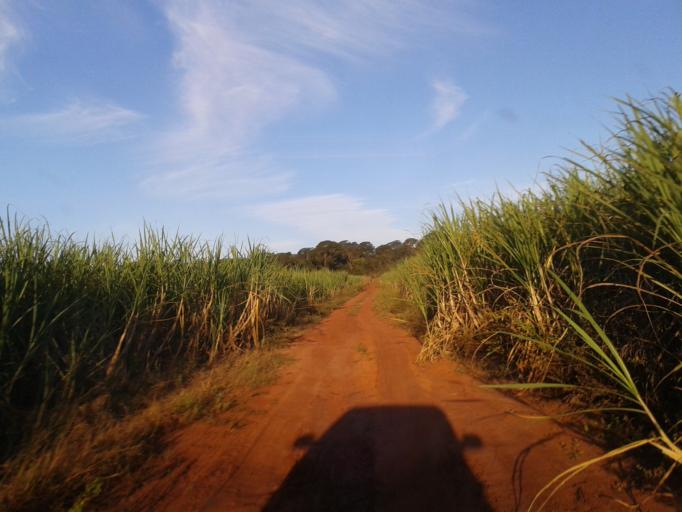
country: BR
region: Minas Gerais
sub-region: Santa Vitoria
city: Santa Vitoria
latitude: -19.0060
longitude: -50.3805
